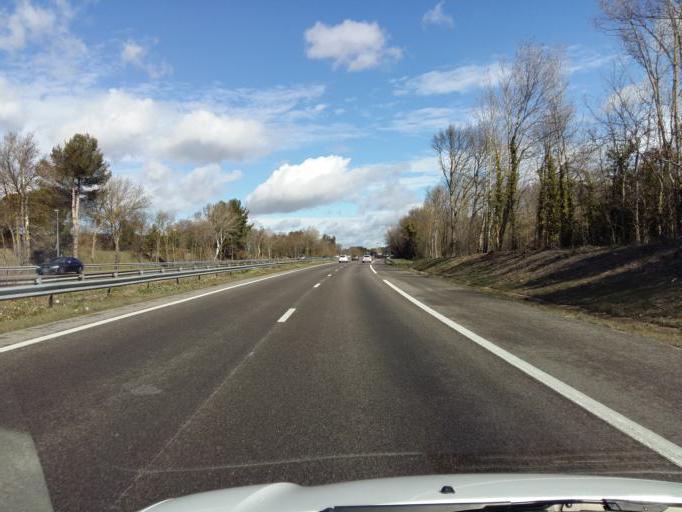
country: FR
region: Provence-Alpes-Cote d'Azur
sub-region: Departement des Bouches-du-Rhone
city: Bouc-Bel-Air
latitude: 43.4548
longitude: 5.3984
